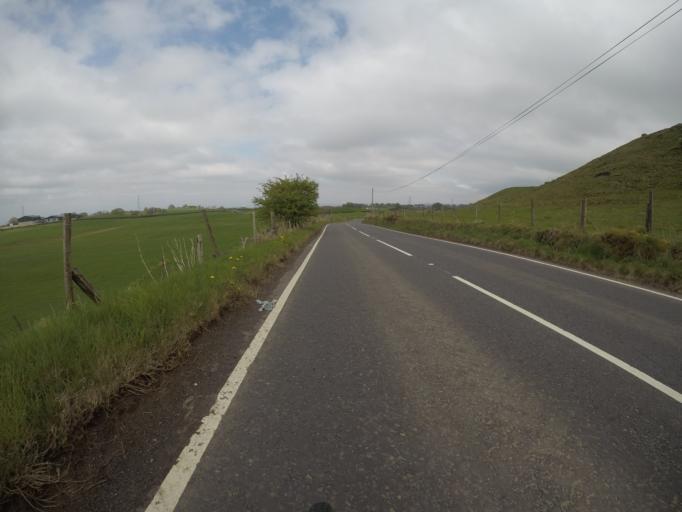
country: GB
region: Scotland
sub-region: East Renfrewshire
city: Barrhead
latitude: 55.7603
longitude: -4.3801
